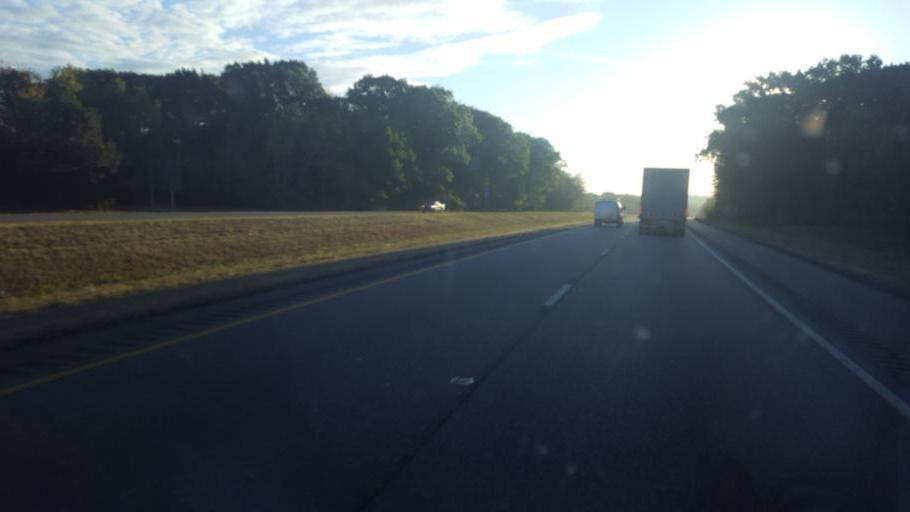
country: US
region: Ohio
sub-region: Trumbull County
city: Churchill
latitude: 41.1597
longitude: -80.6399
